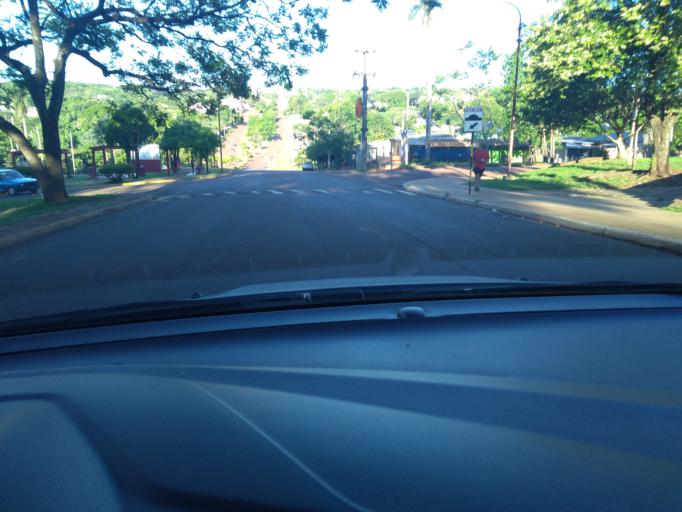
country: AR
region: Misiones
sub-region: Departamento de Obera
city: Obera
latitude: -27.4808
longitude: -55.1090
